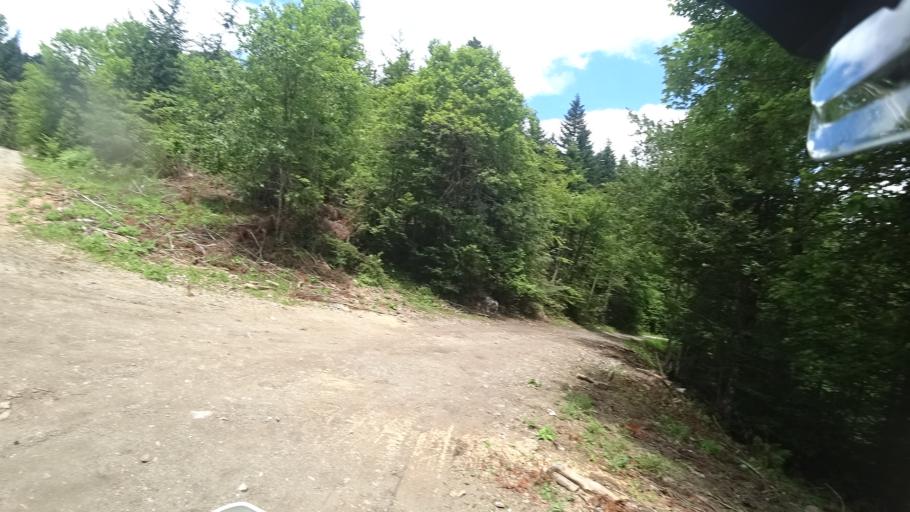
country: SI
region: Osilnica
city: Osilnica
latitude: 45.4944
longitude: 14.7330
